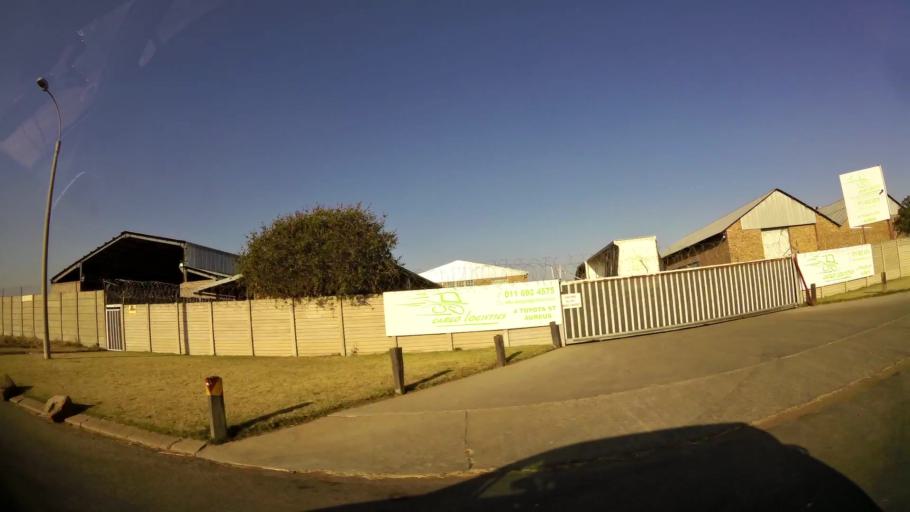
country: ZA
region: Gauteng
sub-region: West Rand District Municipality
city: Randfontein
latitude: -26.2002
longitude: 27.6893
